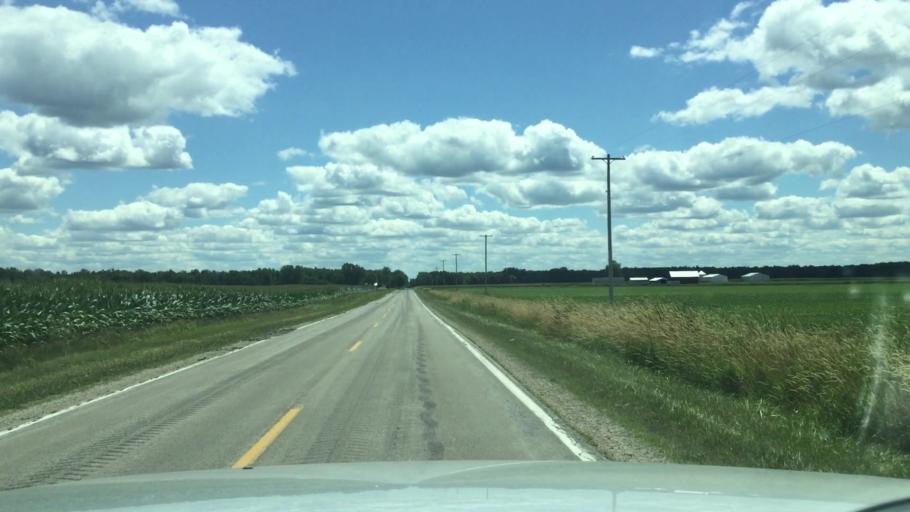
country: US
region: Michigan
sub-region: Saginaw County
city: Saint Charles
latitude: 43.3413
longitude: -84.1899
